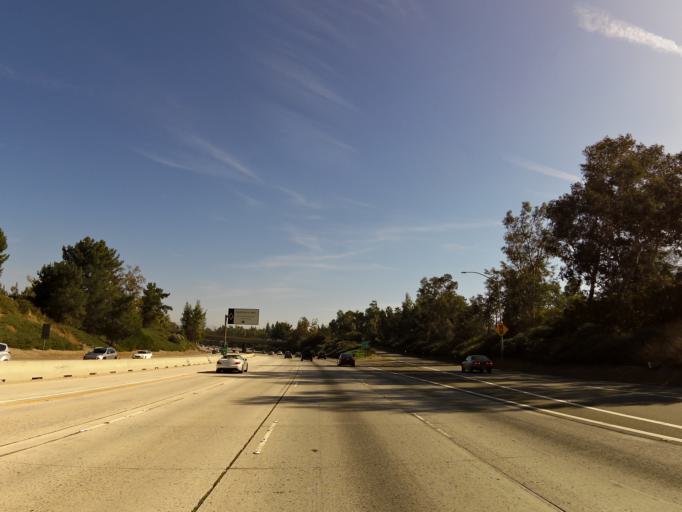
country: US
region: California
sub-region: Los Angeles County
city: Northridge
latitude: 34.2744
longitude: -118.5399
